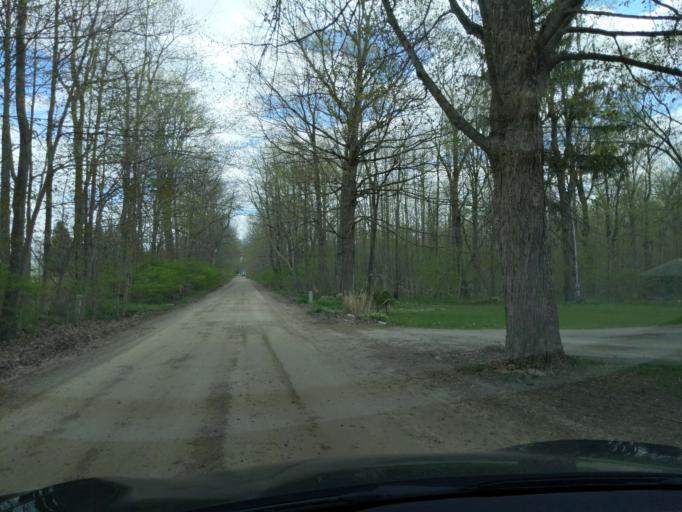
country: US
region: Michigan
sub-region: Eaton County
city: Dimondale
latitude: 42.6274
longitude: -84.6082
